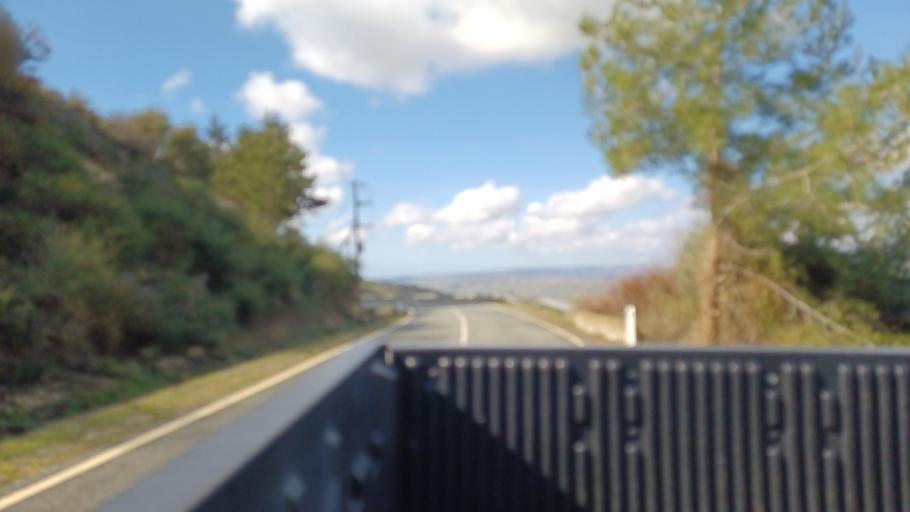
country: CY
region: Limassol
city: Pachna
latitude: 34.7735
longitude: 32.7208
